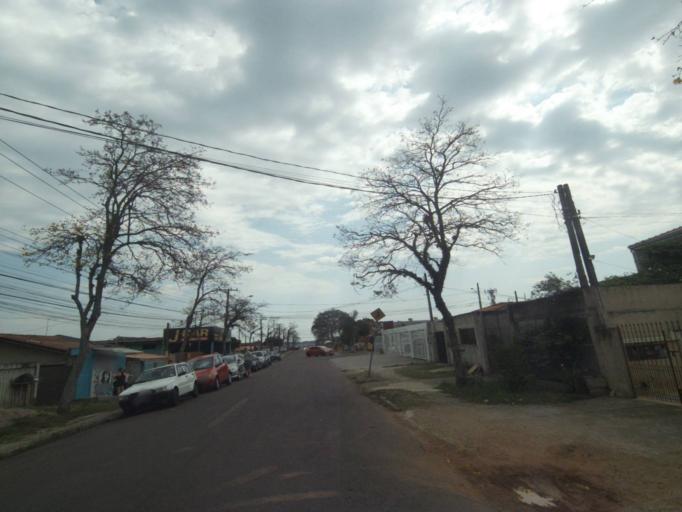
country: BR
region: Parana
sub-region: Sao Jose Dos Pinhais
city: Sao Jose dos Pinhais
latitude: -25.5253
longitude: -49.2586
